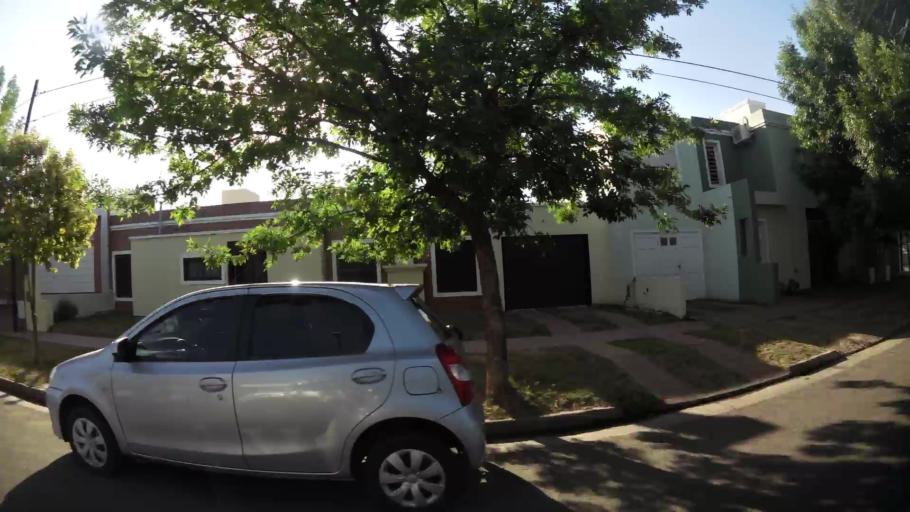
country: AR
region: Cordoba
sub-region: Departamento de Capital
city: Cordoba
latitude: -31.3577
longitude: -64.2129
